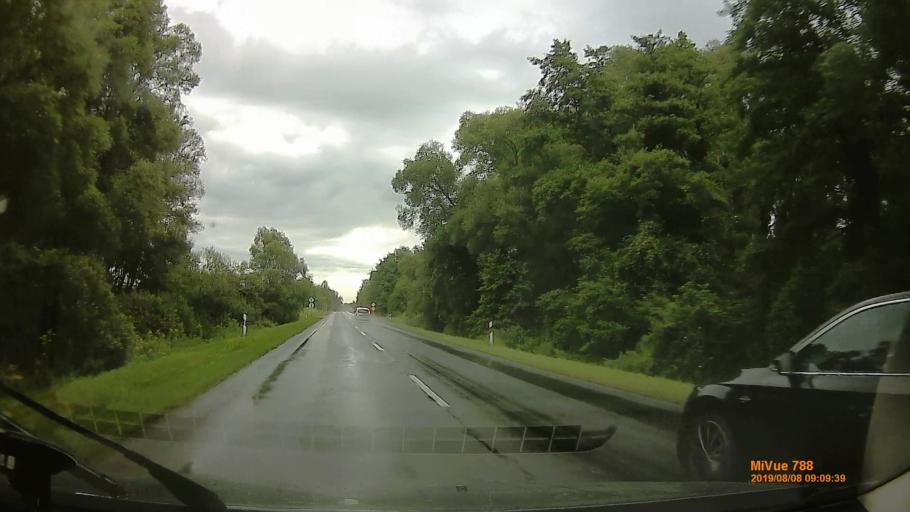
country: HU
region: Zala
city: Zalaegerszeg
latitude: 46.7595
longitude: 16.8578
